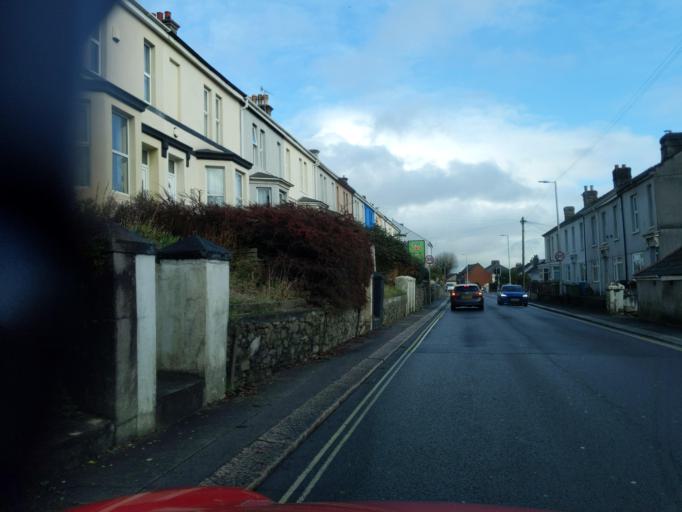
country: GB
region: England
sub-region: Plymouth
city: Plymstock
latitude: 50.3834
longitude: -4.1091
